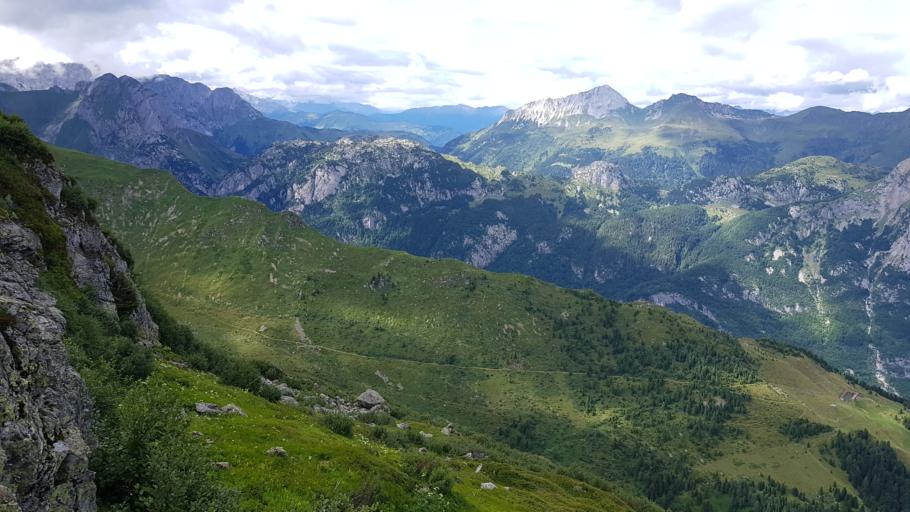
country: IT
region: Friuli Venezia Giulia
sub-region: Provincia di Udine
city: Cercivento
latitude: 46.5626
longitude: 12.9705
